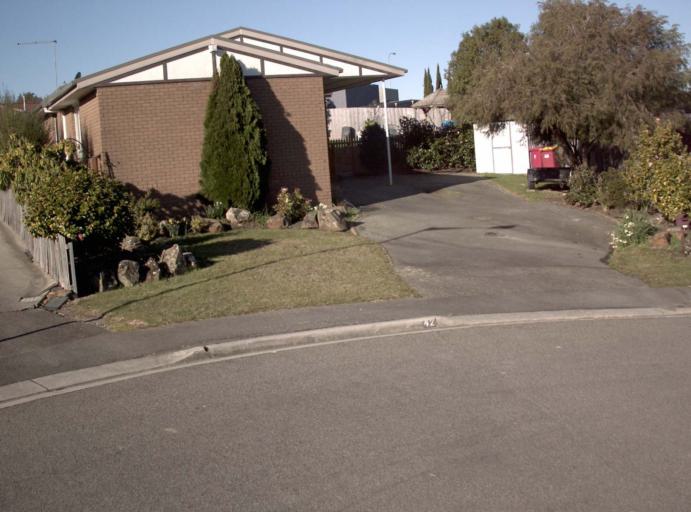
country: AU
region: Tasmania
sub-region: Launceston
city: Summerhill
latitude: -41.4623
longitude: 147.1281
